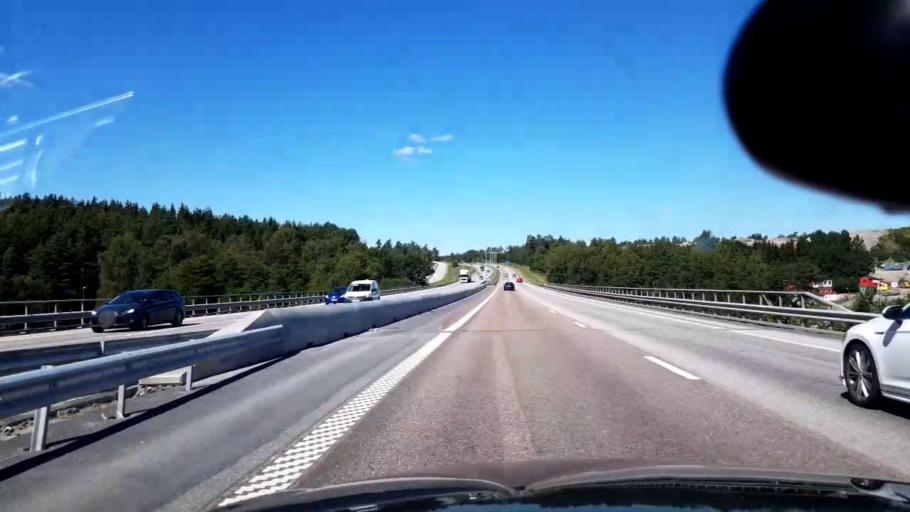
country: SE
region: Stockholm
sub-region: Upplands-Bro Kommun
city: Kungsaengen
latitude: 59.4792
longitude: 17.7881
